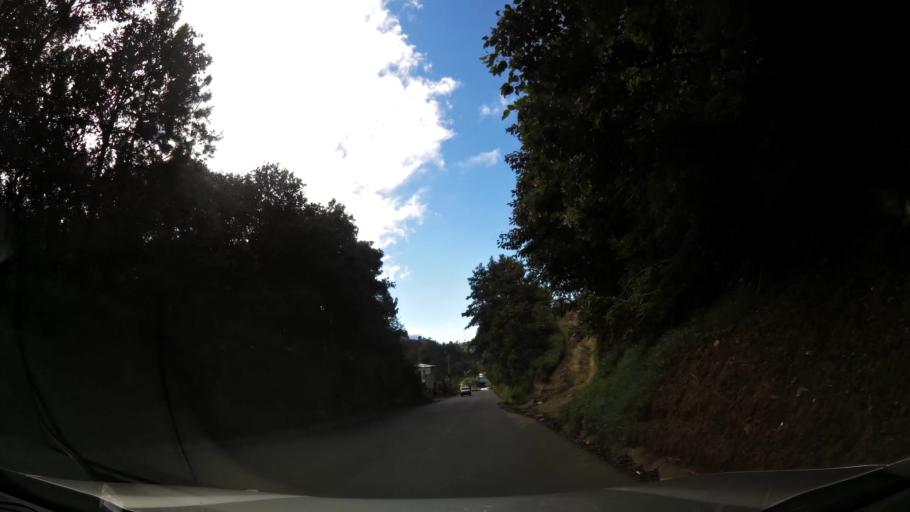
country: GT
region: Solola
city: Concepcion
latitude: 14.8405
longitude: -91.1728
